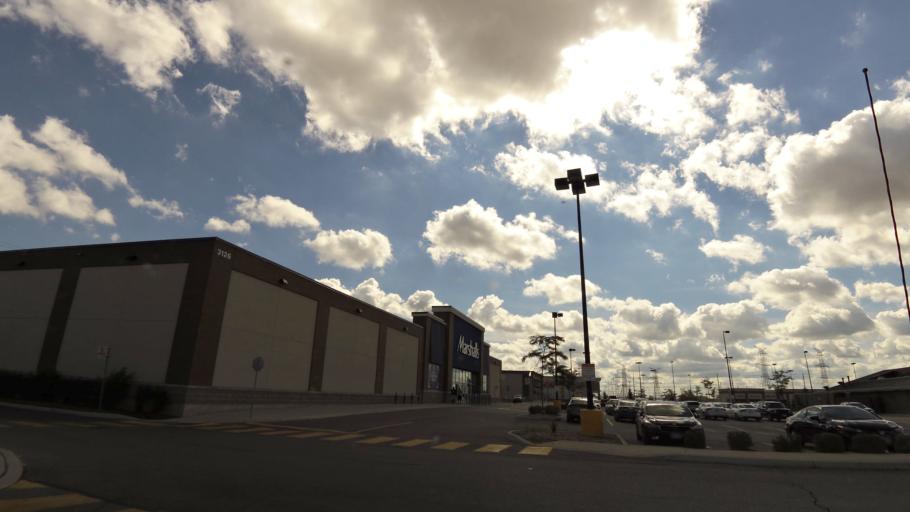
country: CA
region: Ontario
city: Brampton
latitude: 43.5943
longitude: -79.7857
